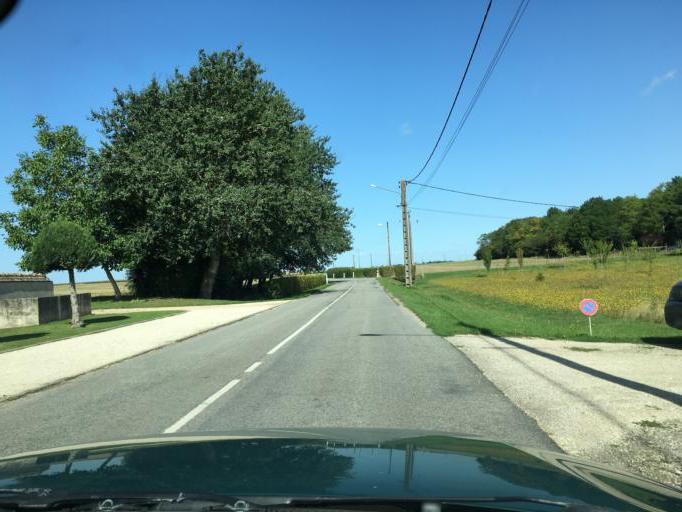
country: FR
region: Centre
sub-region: Departement du Loiret
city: Bricy
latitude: 48.0110
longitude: 1.7383
